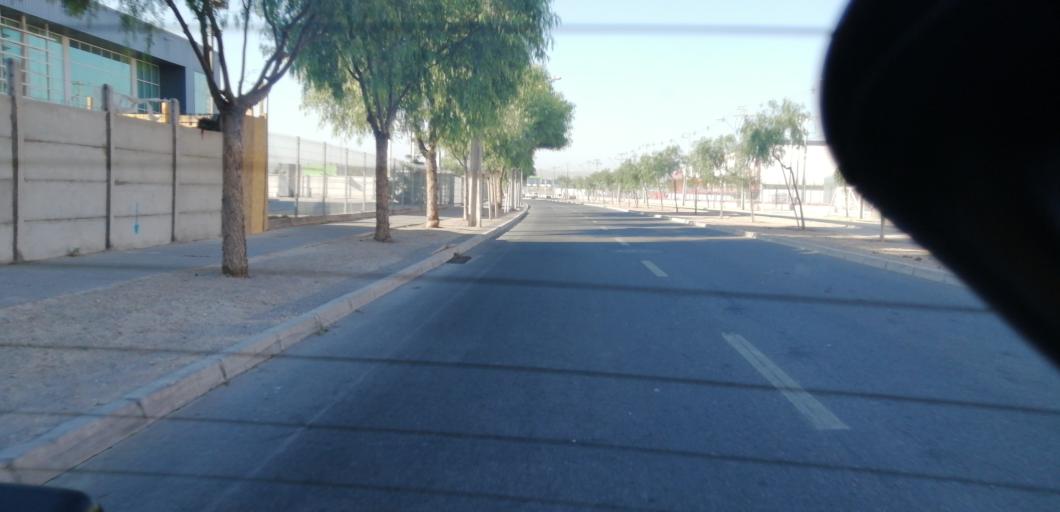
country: CL
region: Santiago Metropolitan
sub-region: Provincia de Santiago
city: Lo Prado
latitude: -33.4333
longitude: -70.7882
